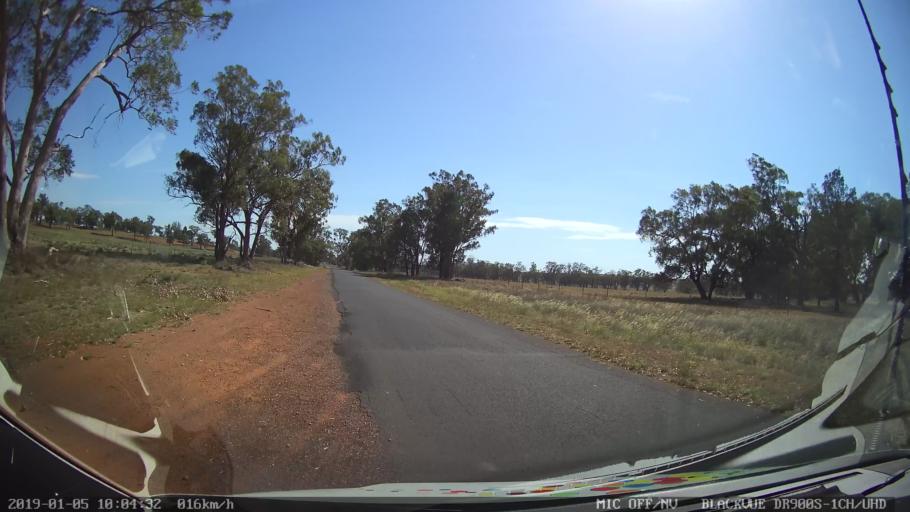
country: AU
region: New South Wales
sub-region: Gilgandra
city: Gilgandra
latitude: -31.6730
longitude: 148.8608
